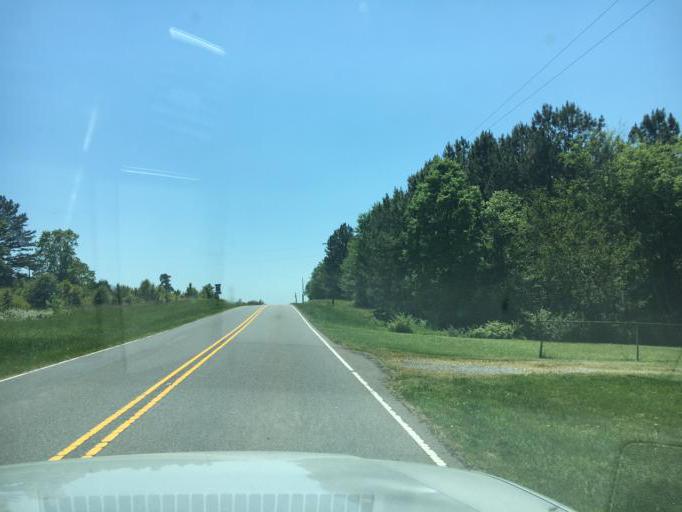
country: US
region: South Carolina
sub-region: Cherokee County
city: Blacksburg
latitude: 35.1762
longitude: -81.5722
